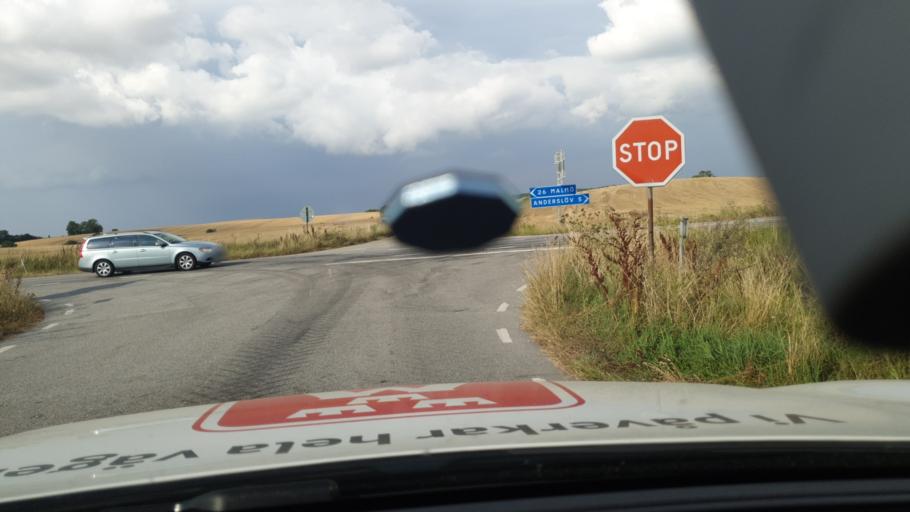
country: SE
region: Skane
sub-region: Svedala Kommun
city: Svedala
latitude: 55.4512
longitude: 13.2462
